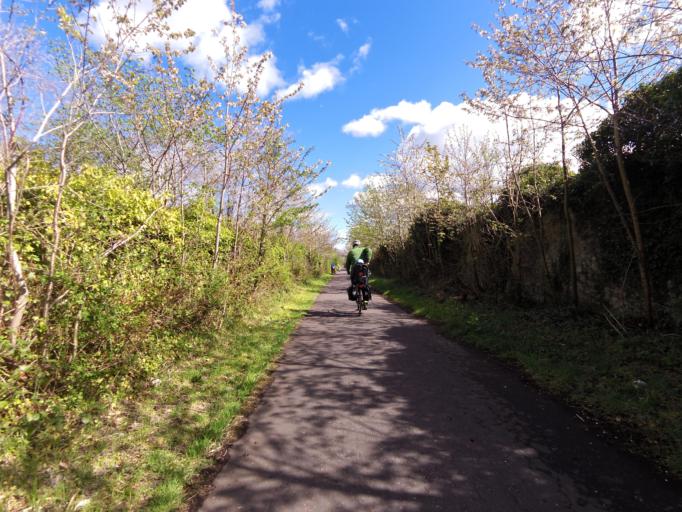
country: GB
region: Scotland
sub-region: West Lothian
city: Seafield
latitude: 55.9373
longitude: -3.1490
